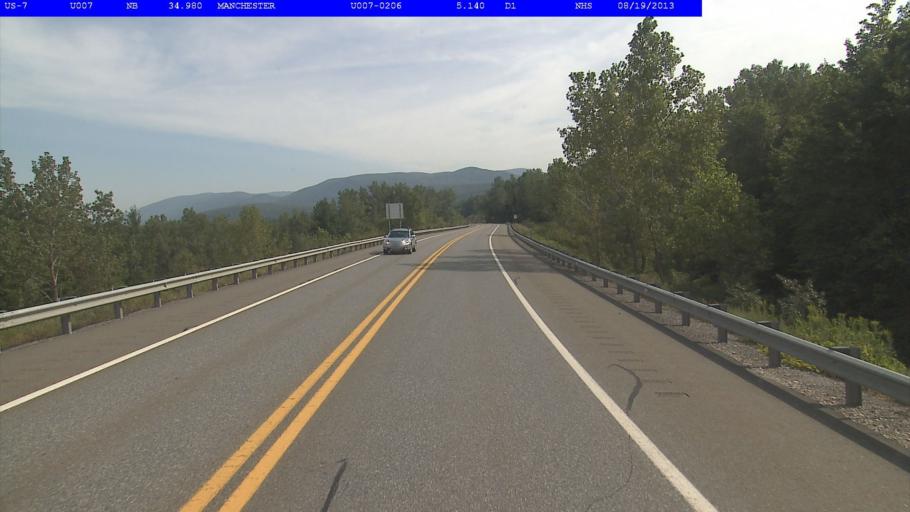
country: US
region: Vermont
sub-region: Bennington County
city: Manchester Center
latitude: 43.1791
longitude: -73.0253
